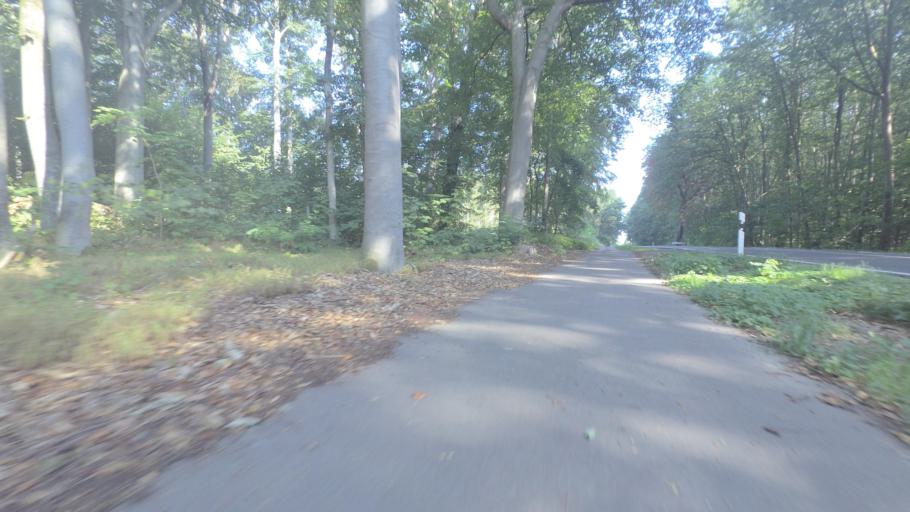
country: DE
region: Mecklenburg-Vorpommern
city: Malchow
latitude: 53.5030
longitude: 12.4220
